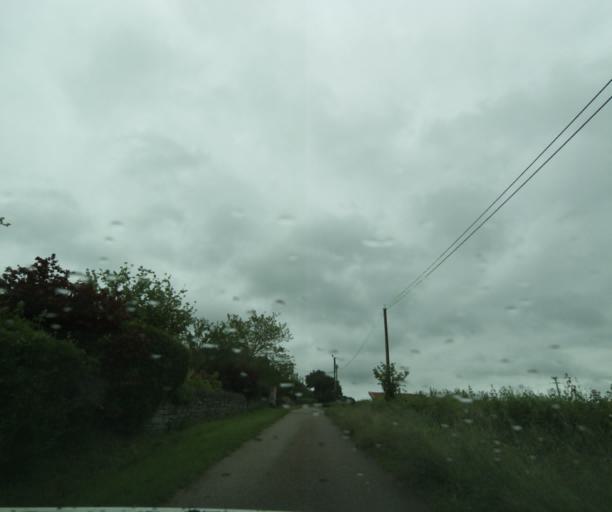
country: FR
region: Bourgogne
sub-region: Departement de Saone-et-Loire
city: Charolles
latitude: 46.4901
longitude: 4.2597
